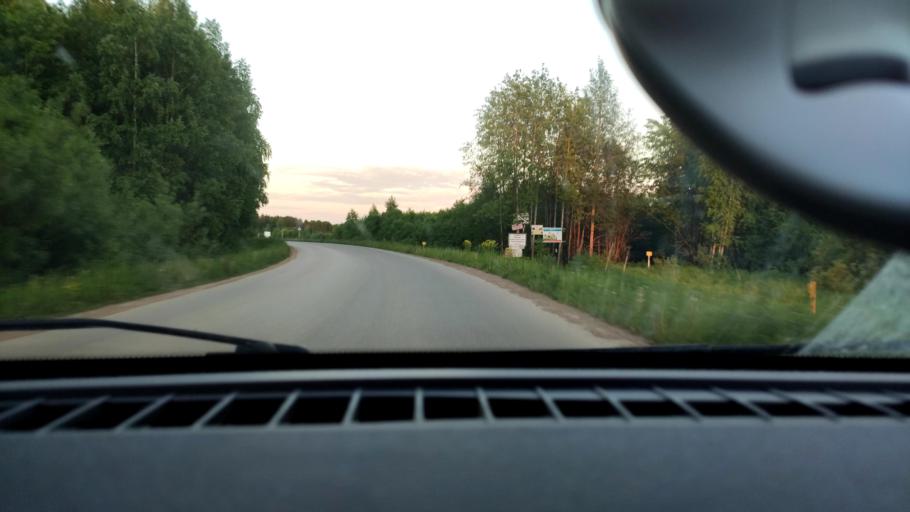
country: RU
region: Perm
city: Polazna
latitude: 58.2028
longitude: 56.4723
